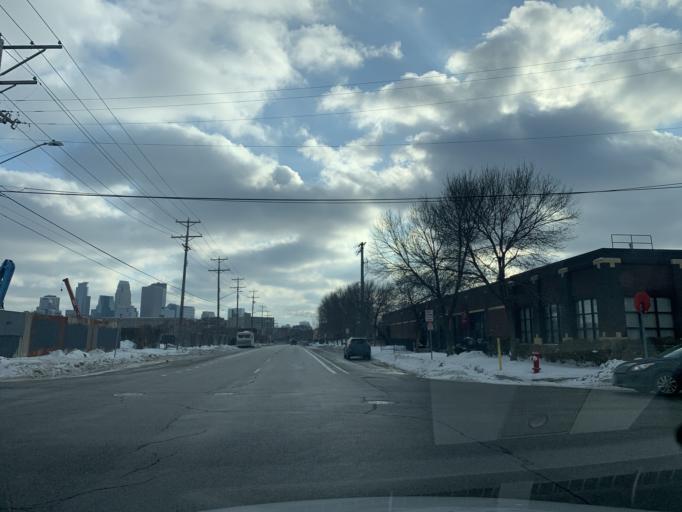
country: US
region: Minnesota
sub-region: Hennepin County
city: Minneapolis
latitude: 44.9959
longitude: -93.2801
